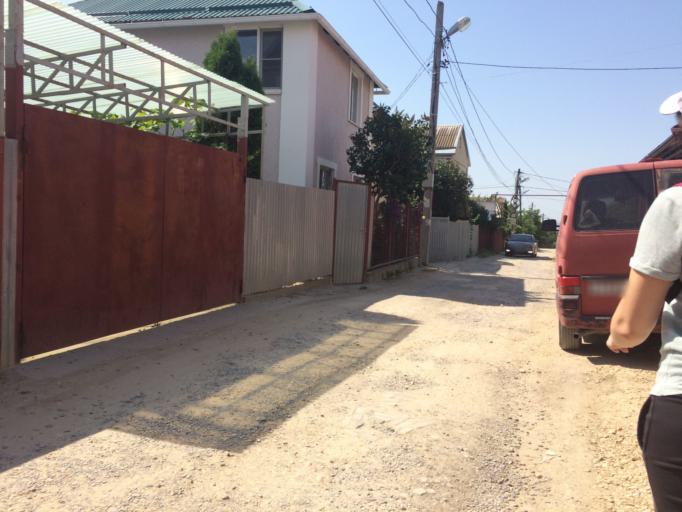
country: RU
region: Stavropol'skiy
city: Tatarka
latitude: 44.9852
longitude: 41.9419
